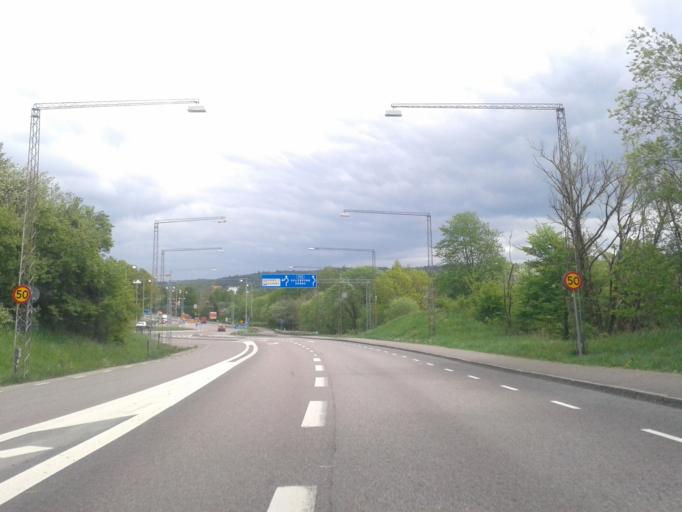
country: SE
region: Vaestra Goetaland
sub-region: Goteborg
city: Eriksbo
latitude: 57.7723
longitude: 12.0476
